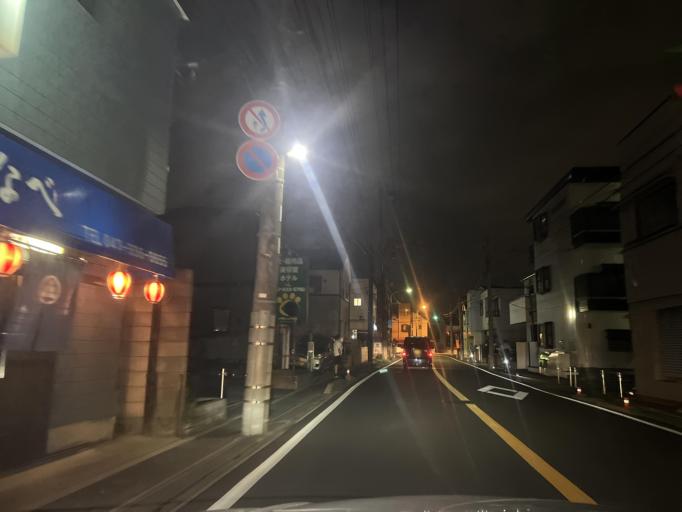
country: JP
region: Chiba
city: Matsudo
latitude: 35.7308
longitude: 139.9298
